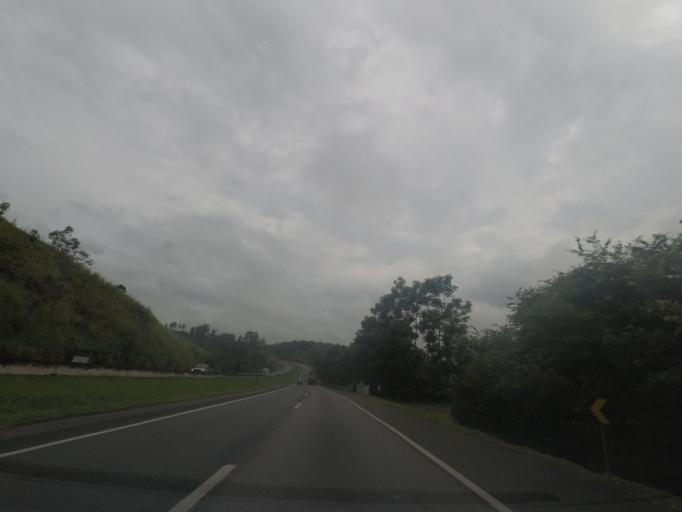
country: BR
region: Sao Paulo
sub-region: Cajati
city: Cajati
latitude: -24.7554
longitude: -48.1619
